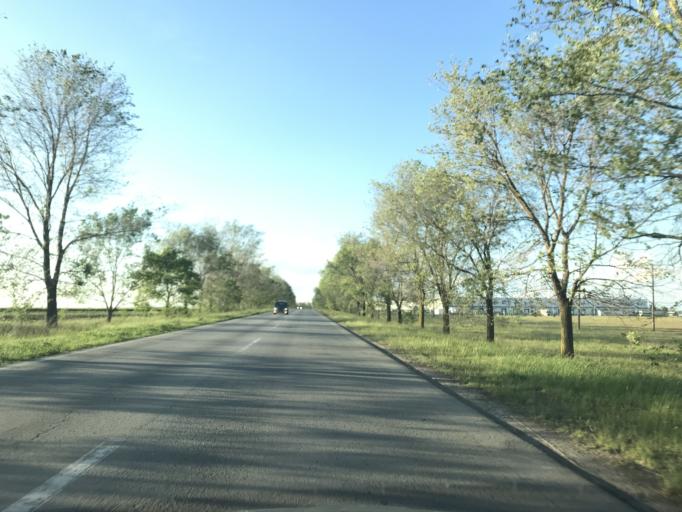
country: RS
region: Autonomna Pokrajina Vojvodina
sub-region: Srednjebanatski Okrug
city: Zrenjanin
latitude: 45.3839
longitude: 20.3517
